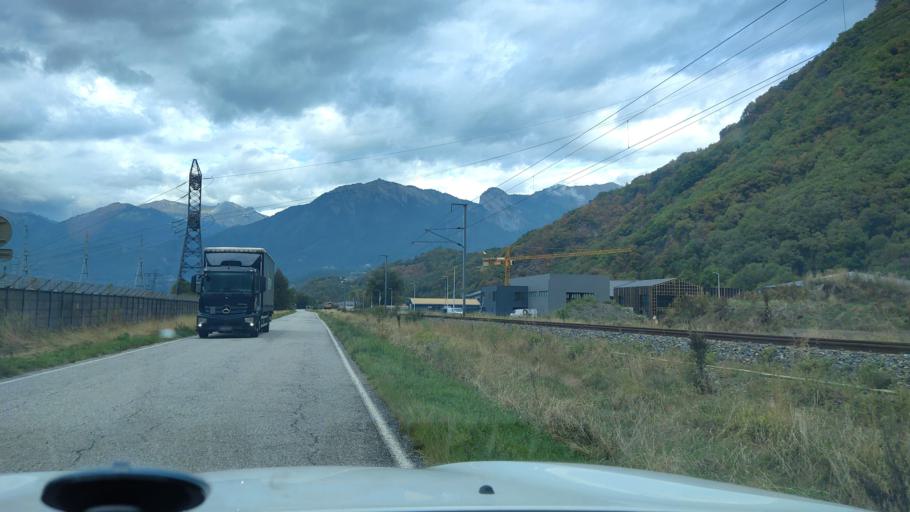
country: FR
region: Rhone-Alpes
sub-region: Departement de la Savoie
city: Albertville
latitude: 45.6630
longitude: 6.4201
